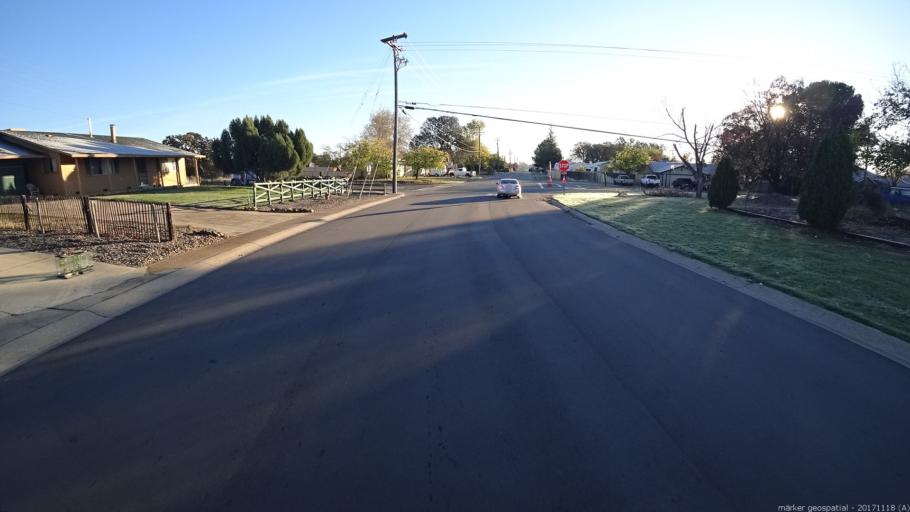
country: US
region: California
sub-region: Shasta County
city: Cottonwood
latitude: 40.3977
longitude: -122.2896
